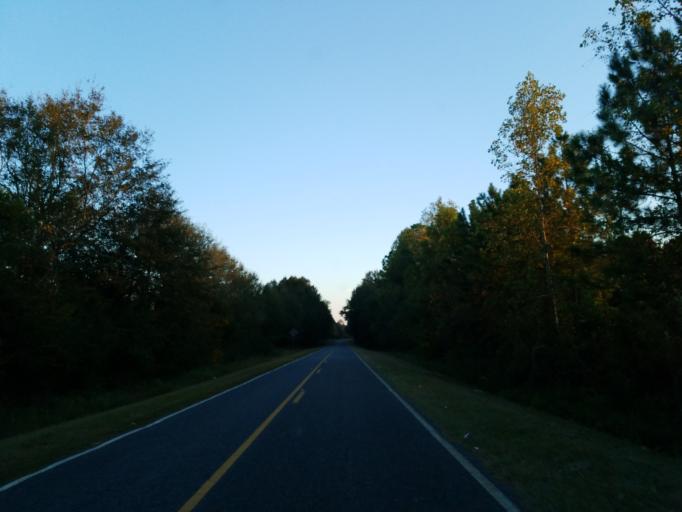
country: US
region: Georgia
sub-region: Ben Hill County
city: Fitzgerald
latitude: 31.6656
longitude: -83.3940
